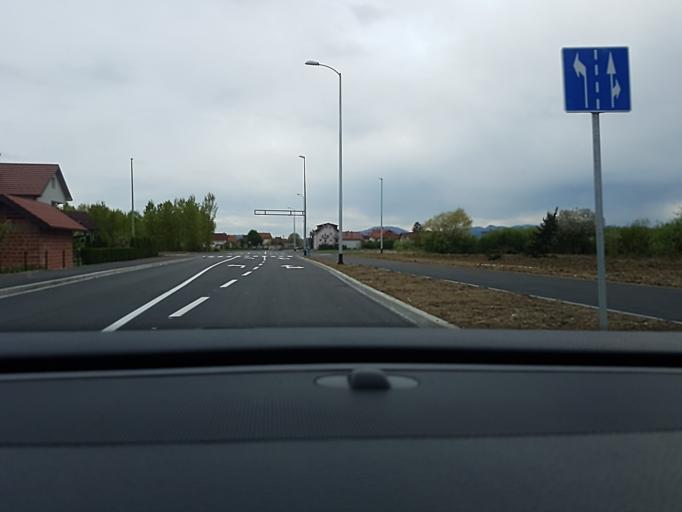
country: HR
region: Zagrebacka
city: Zapresic
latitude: 45.8582
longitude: 15.7981
